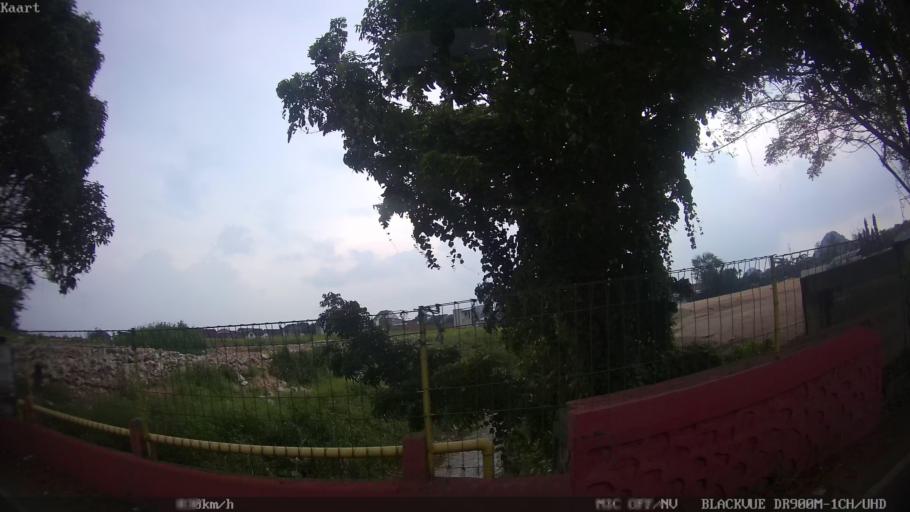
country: ID
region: Lampung
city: Kedaton
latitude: -5.3984
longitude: 105.2814
